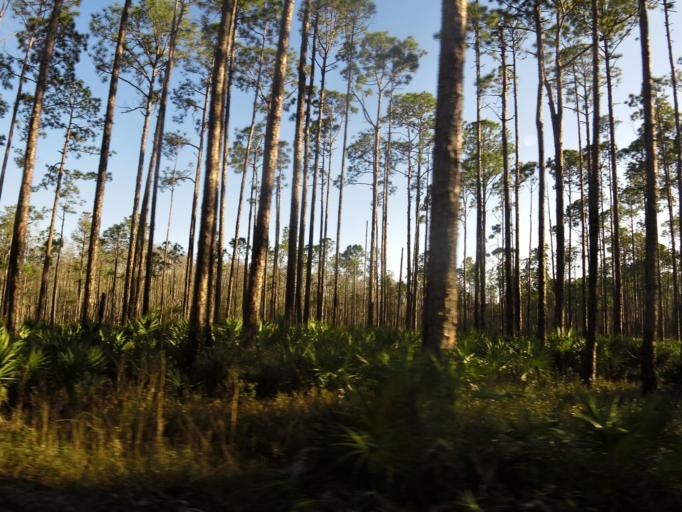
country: US
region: Florida
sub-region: Clay County
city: Middleburg
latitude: 30.1480
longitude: -81.8983
